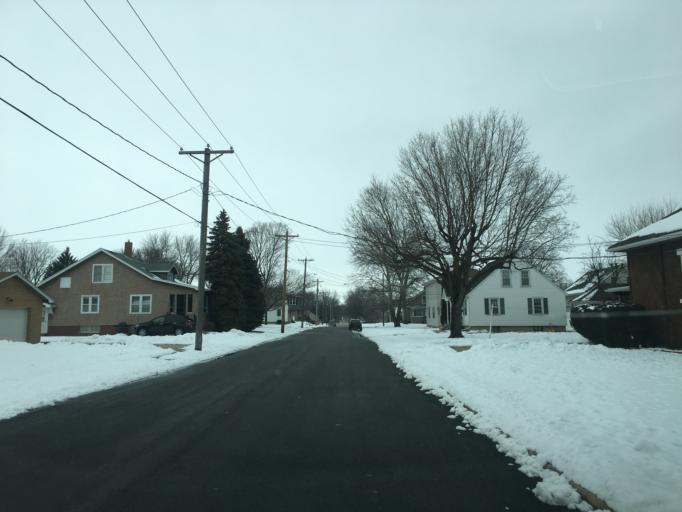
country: US
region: Illinois
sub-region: LaSalle County
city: Peru
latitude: 41.3313
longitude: -89.1318
